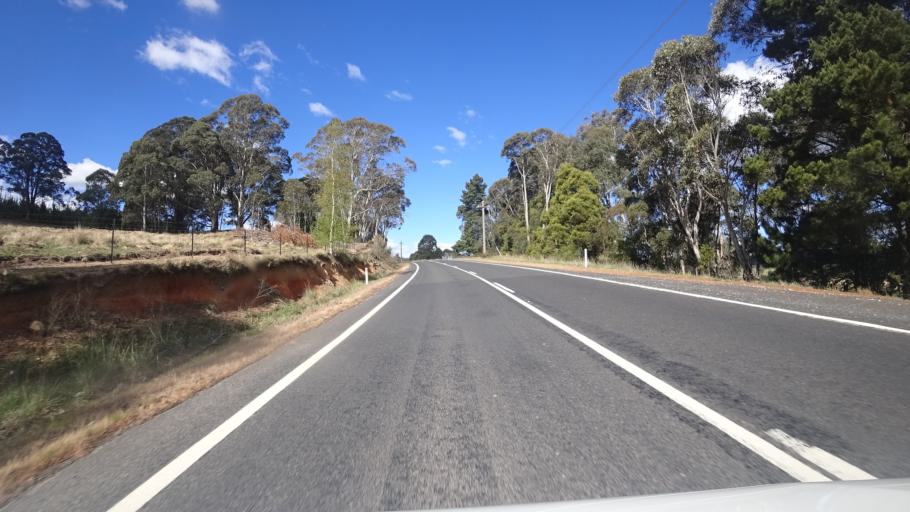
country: AU
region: New South Wales
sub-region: Oberon
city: Oberon
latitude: -33.6823
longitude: 150.0387
